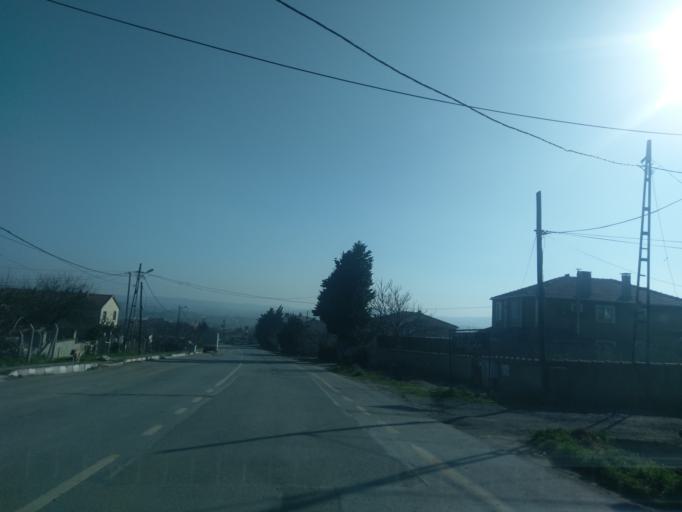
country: TR
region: Istanbul
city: Catalca
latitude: 41.1177
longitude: 28.4502
